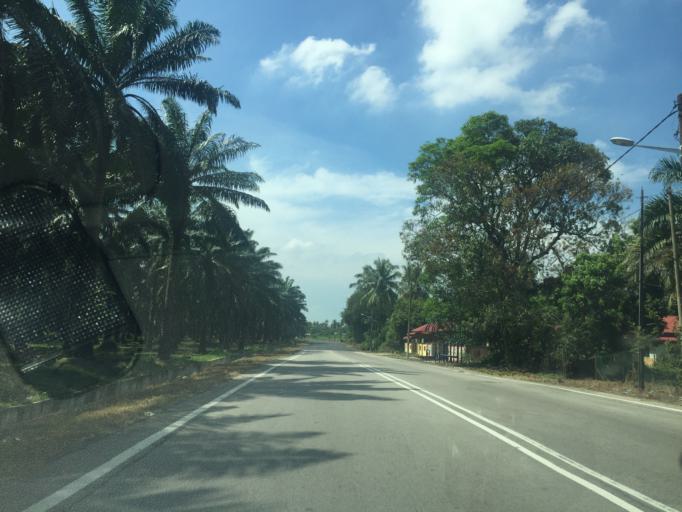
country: MY
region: Penang
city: Tasek Glugor
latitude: 5.4941
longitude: 100.5091
